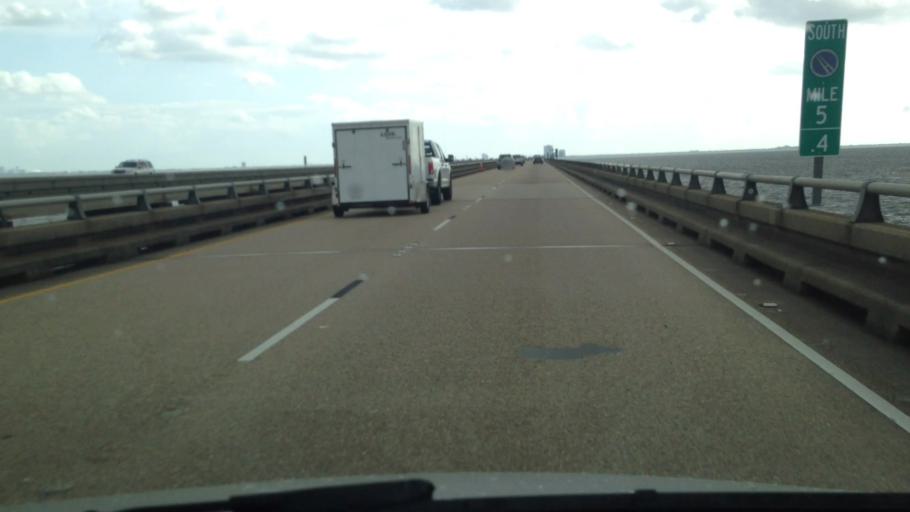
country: US
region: Louisiana
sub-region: Jefferson Parish
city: Metairie
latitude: 30.0993
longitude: -90.1405
